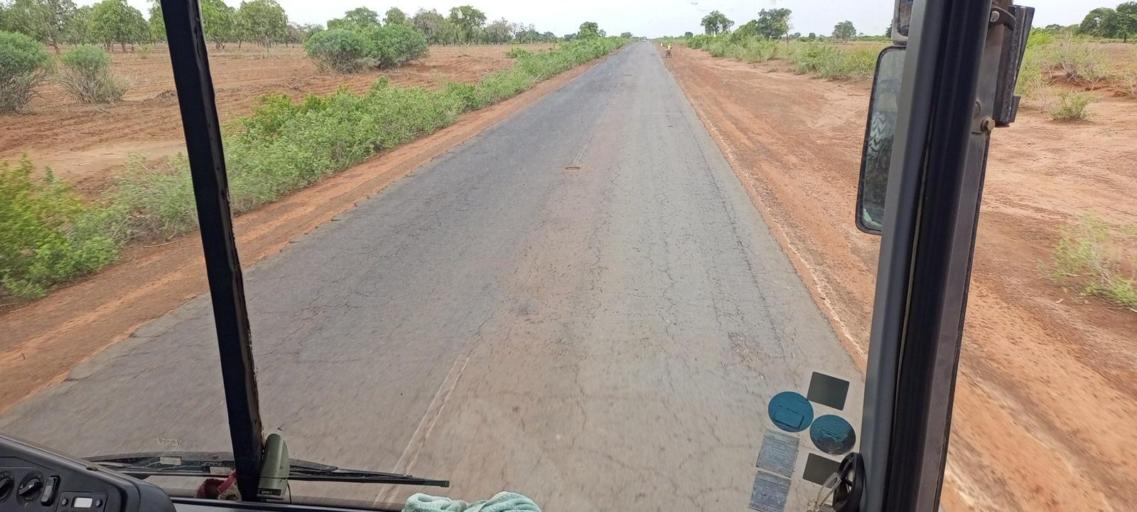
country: ML
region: Segou
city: Bla
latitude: 12.7167
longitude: -5.7248
